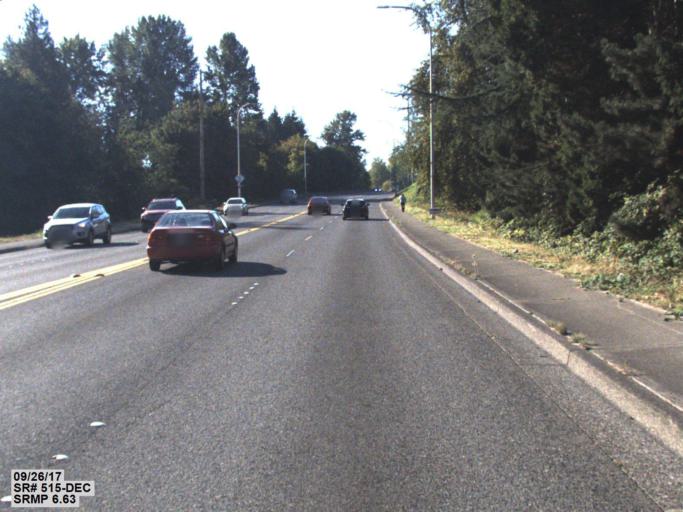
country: US
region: Washington
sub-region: King County
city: Renton
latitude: 47.4647
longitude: -122.2075
